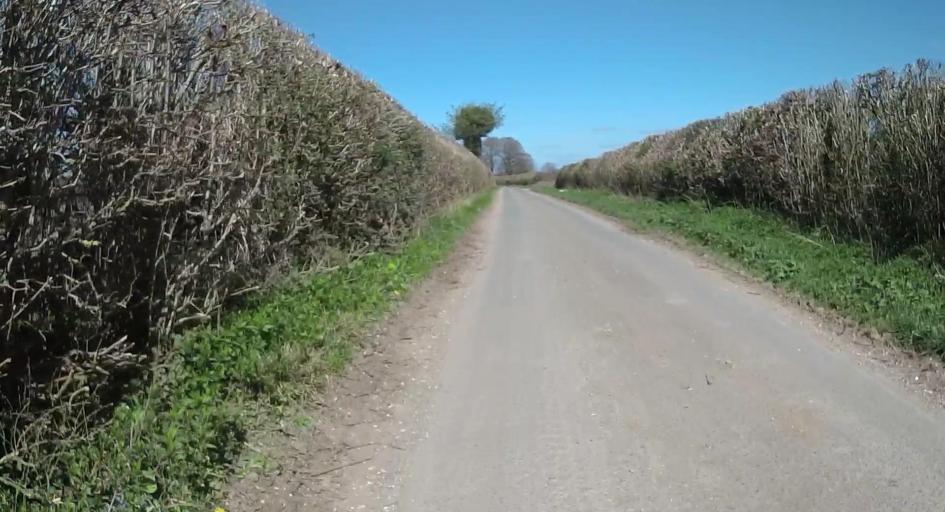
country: GB
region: England
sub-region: Hampshire
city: Kingsclere
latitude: 51.2786
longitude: -1.1835
